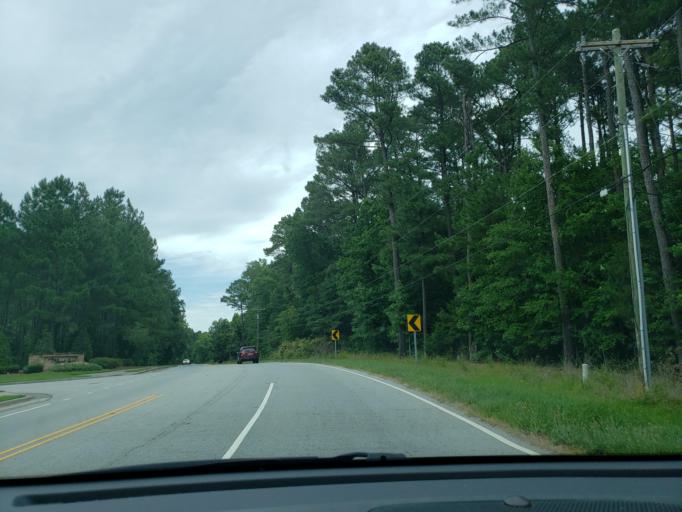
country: US
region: North Carolina
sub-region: Orange County
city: Chapel Hill
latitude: 35.8840
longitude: -78.9910
